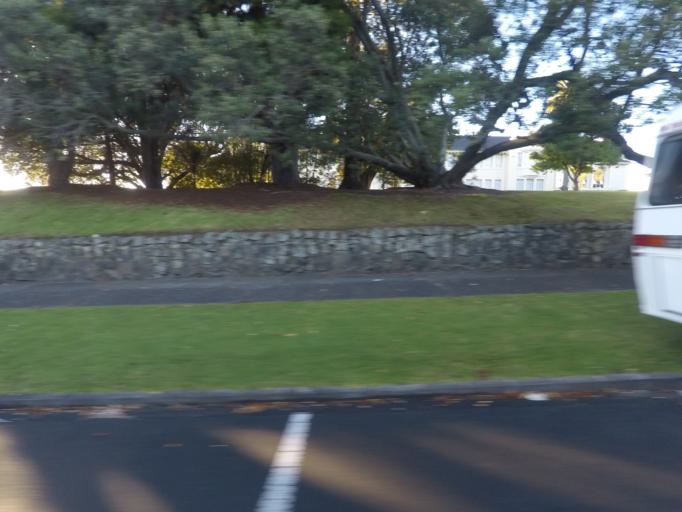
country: NZ
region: Auckland
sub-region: Auckland
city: Auckland
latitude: -36.8842
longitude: 174.7249
